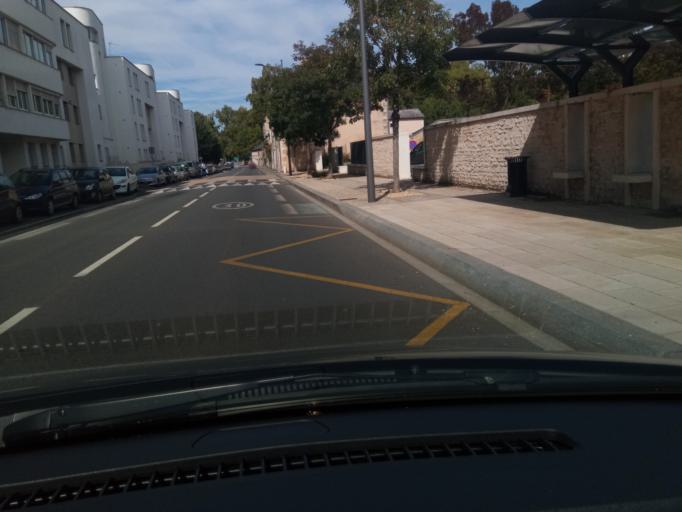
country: FR
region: Poitou-Charentes
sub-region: Departement de la Vienne
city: Poitiers
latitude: 46.5824
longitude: 0.3525
